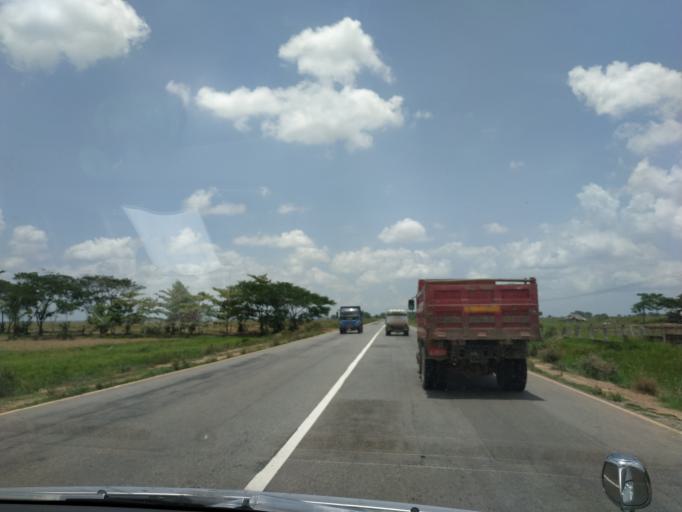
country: MM
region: Bago
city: Bago
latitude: 17.4646
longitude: 96.5888
